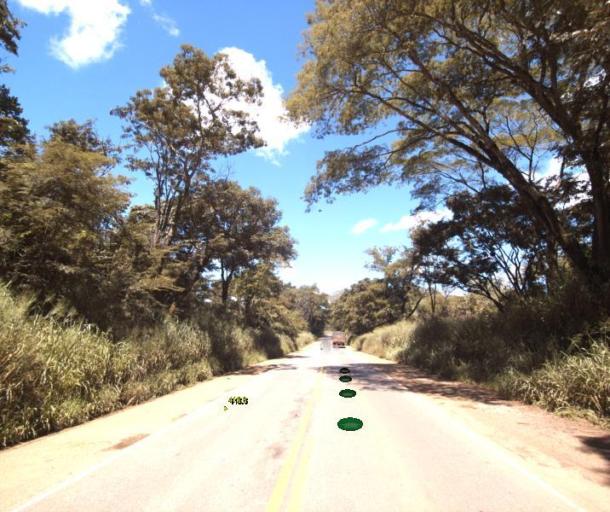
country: BR
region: Goias
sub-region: Anapolis
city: Anapolis
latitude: -16.1299
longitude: -49.0466
